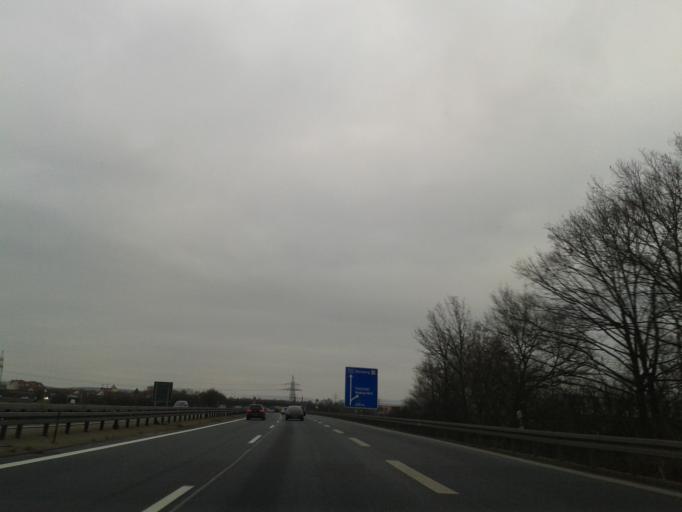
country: DE
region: Bavaria
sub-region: Upper Franconia
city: Hallstadt
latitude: 49.9183
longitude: 10.8641
